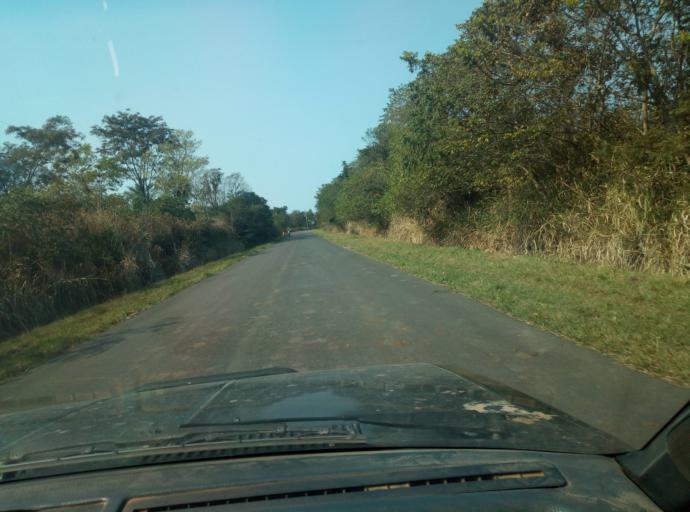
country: PY
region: Caaguazu
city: Carayao
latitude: -25.1887
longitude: -56.3120
